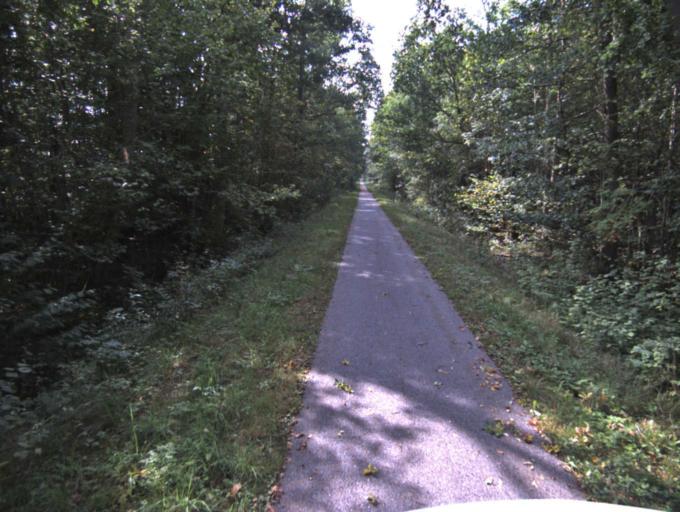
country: SE
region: Vaestra Goetaland
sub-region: Tranemo Kommun
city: Limmared
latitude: 57.6315
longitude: 13.3514
